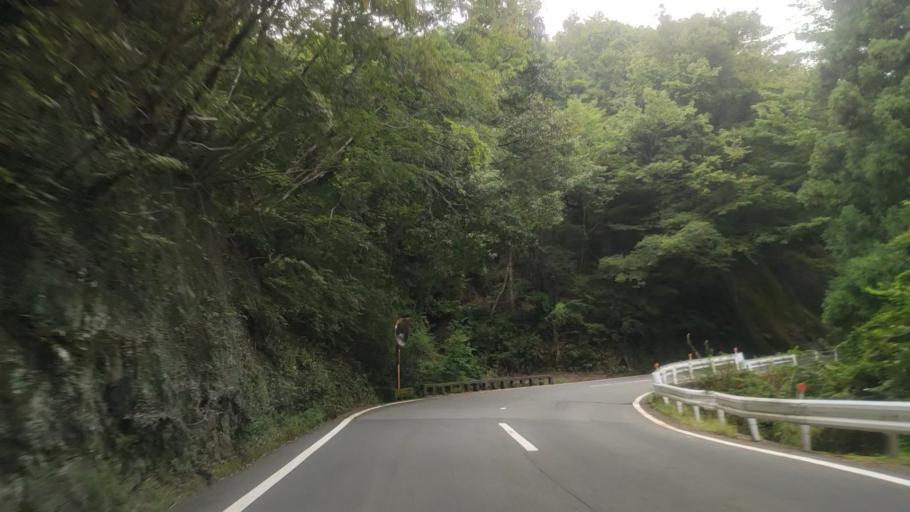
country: JP
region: Wakayama
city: Koya
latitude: 34.2140
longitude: 135.5403
